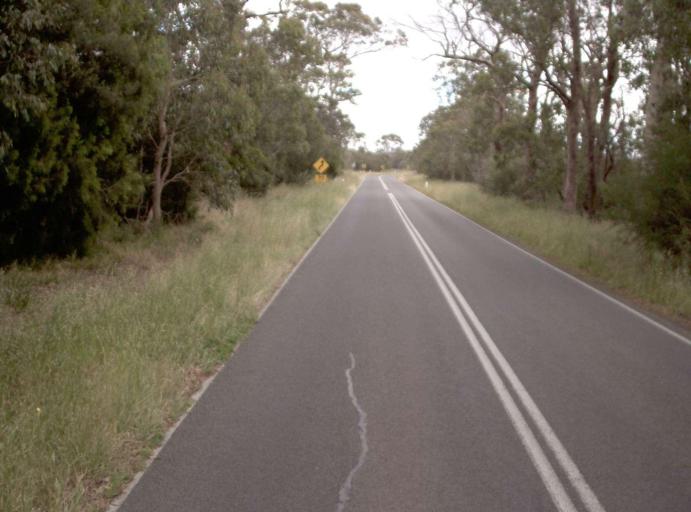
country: AU
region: Victoria
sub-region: Latrobe
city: Moe
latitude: -38.1330
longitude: 146.2581
